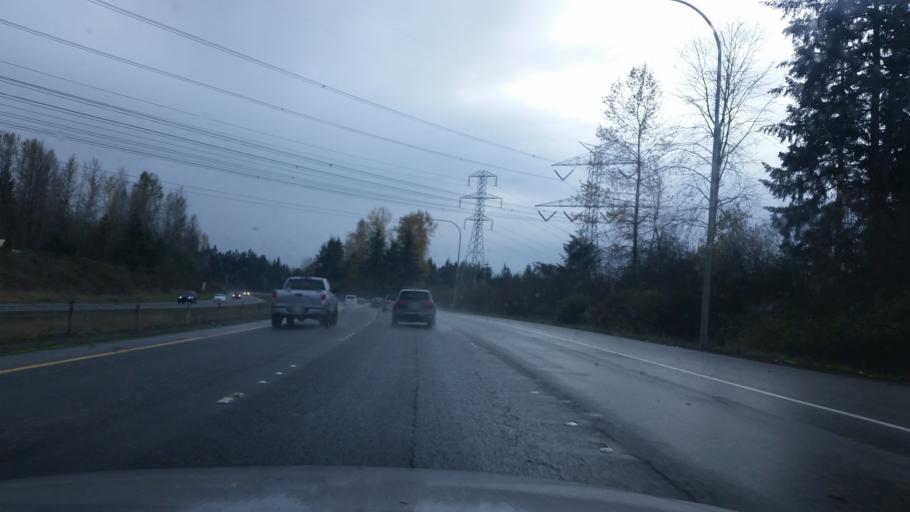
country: US
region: Washington
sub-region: King County
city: Covington
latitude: 47.3435
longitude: -122.1460
